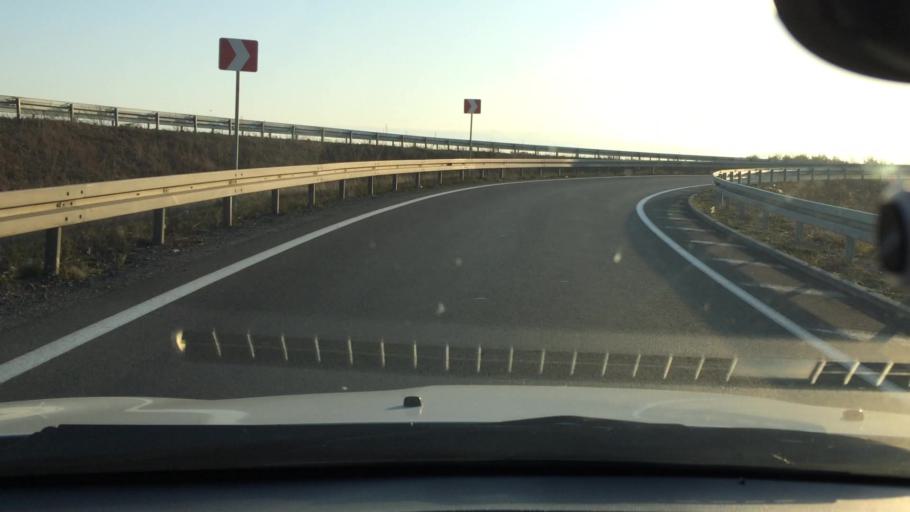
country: GE
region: Shida Kartli
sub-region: Khashuris Raioni
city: Khashuri
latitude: 42.0121
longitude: 43.6996
